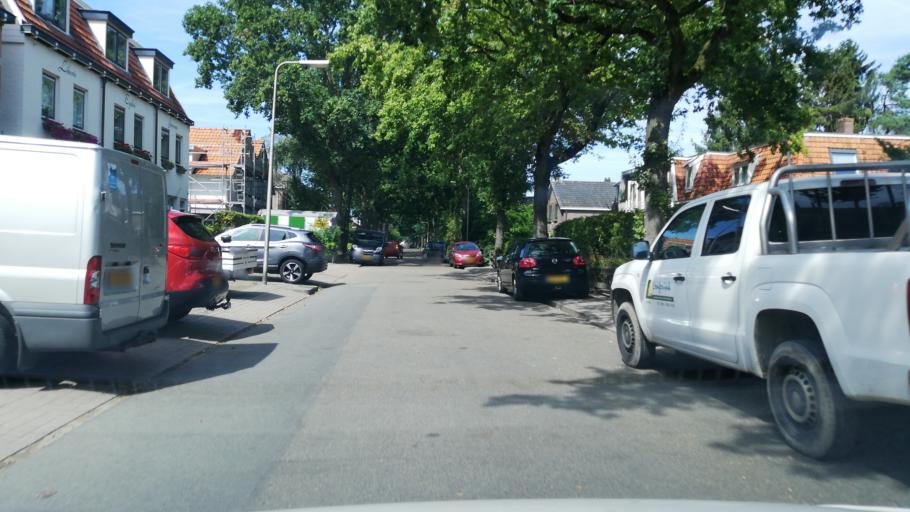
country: NL
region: Overijssel
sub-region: Gemeente Zwolle
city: Zwolle
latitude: 52.4953
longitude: 6.1033
